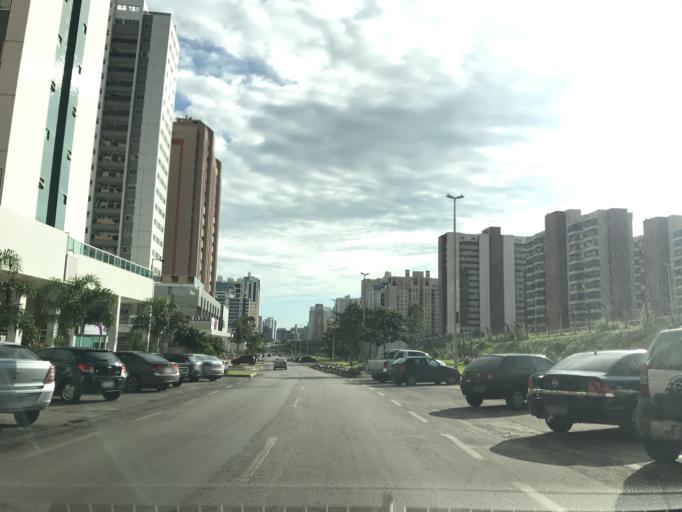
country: BR
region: Federal District
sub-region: Brasilia
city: Brasilia
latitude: -15.8396
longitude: -48.0246
